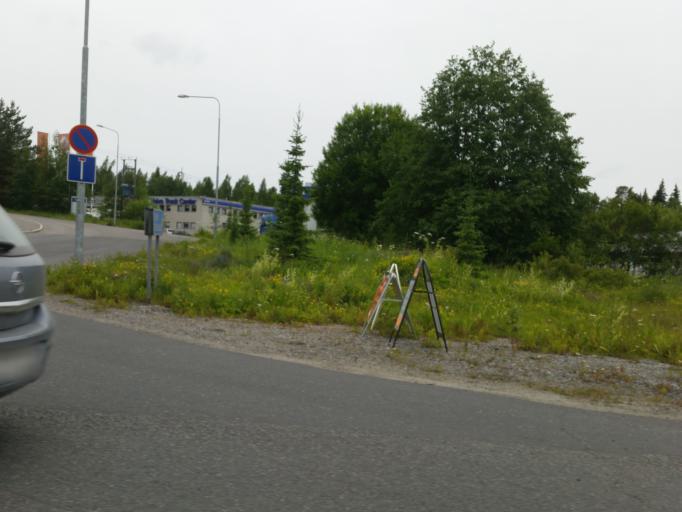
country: FI
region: Northern Savo
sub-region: Kuopio
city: Kuopio
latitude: 62.8709
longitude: 27.6249
